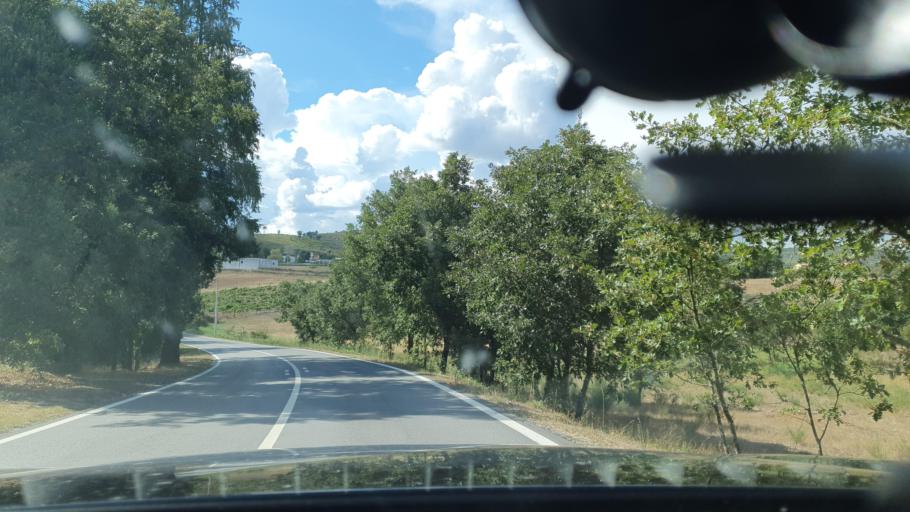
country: PT
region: Vila Real
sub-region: Chaves
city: Chaves
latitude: 41.7115
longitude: -7.5571
